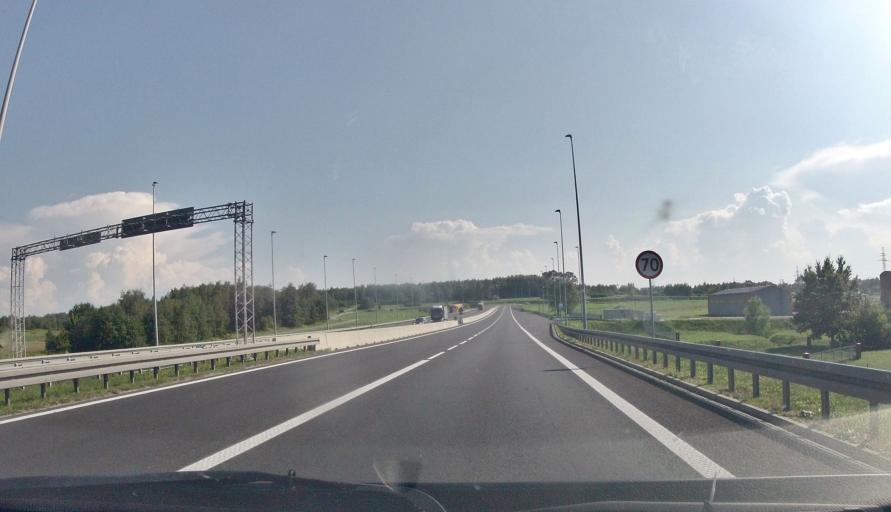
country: PL
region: Lesser Poland Voivodeship
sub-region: Powiat tarnowski
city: Lisia Gora
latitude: 50.0524
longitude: 21.0141
